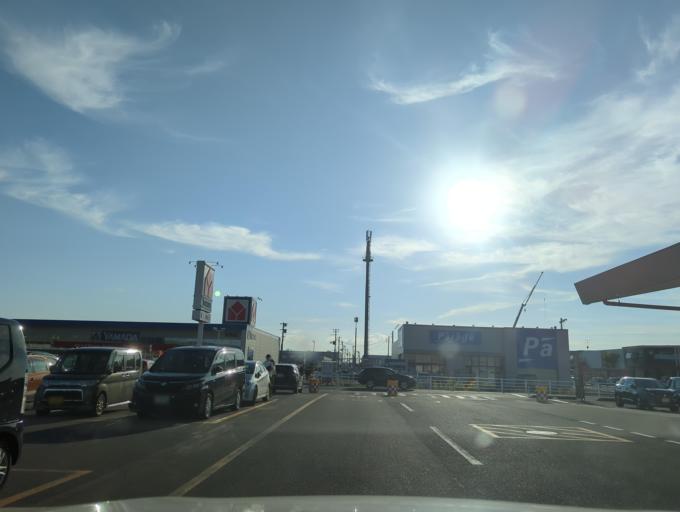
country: JP
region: Niigata
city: Mitsuke
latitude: 37.5390
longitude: 138.8890
